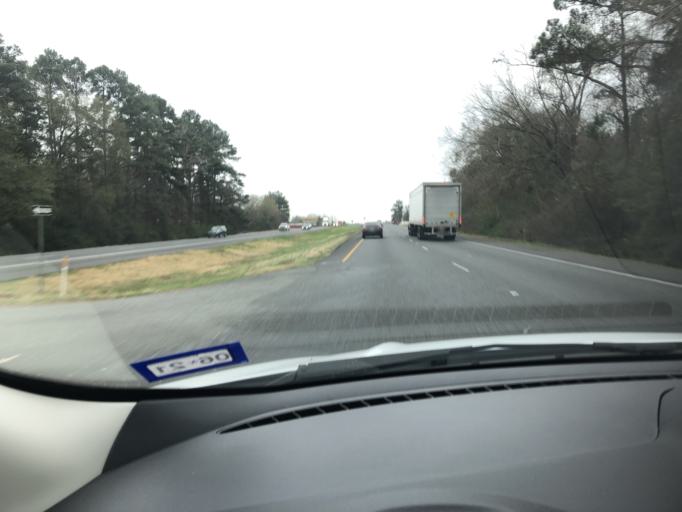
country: US
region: Texas
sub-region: Angelina County
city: Redland
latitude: 31.4687
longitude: -94.7265
